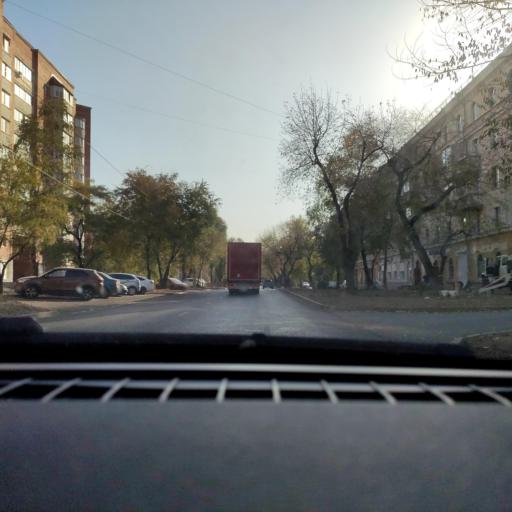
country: RU
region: Voronezj
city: Voronezh
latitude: 51.6379
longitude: 39.2386
